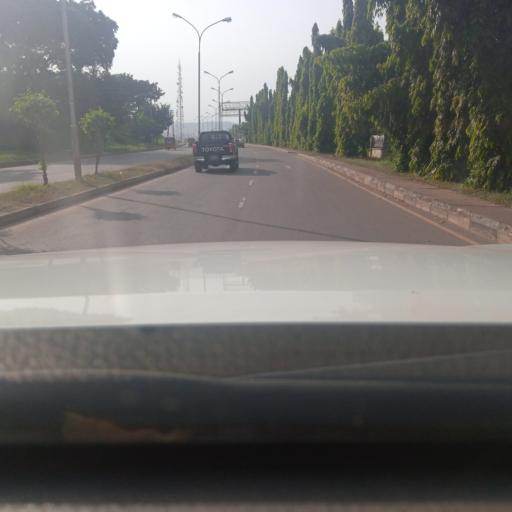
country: NG
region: Enugu
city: Enugu
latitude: 6.4407
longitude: 7.5130
